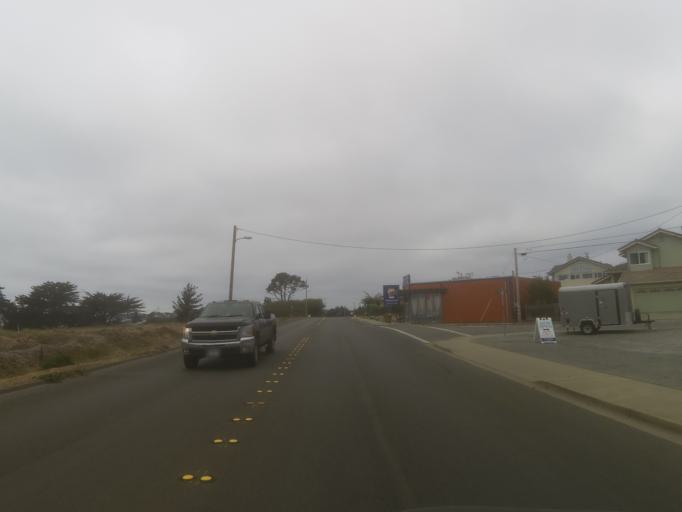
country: US
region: California
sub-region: San Mateo County
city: El Granada
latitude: 37.5040
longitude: -122.4758
